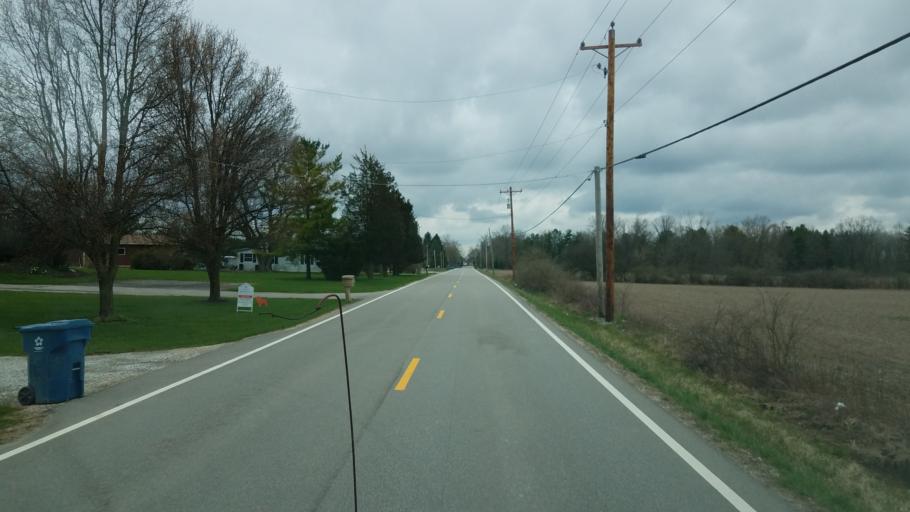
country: US
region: Ohio
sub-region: Delaware County
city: Powell
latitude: 40.2227
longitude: -83.1326
